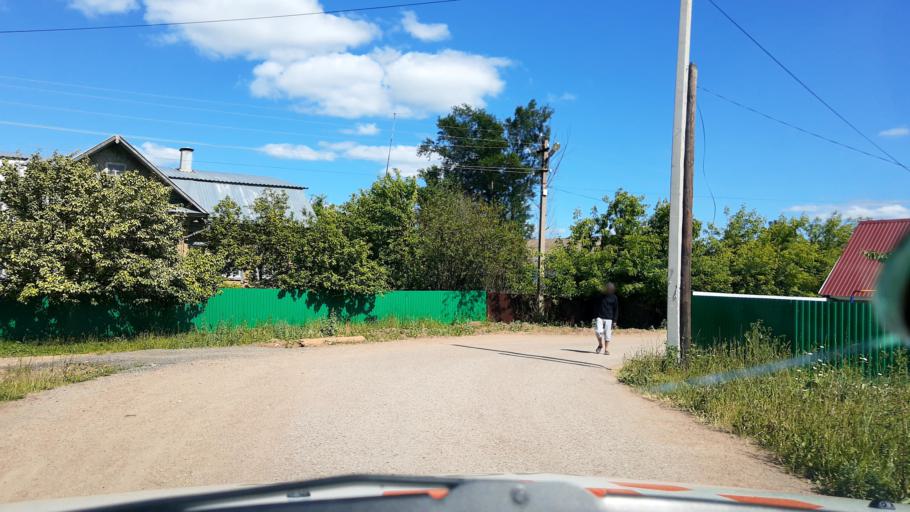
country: RU
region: Bashkortostan
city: Iglino
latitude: 54.8392
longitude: 56.4220
